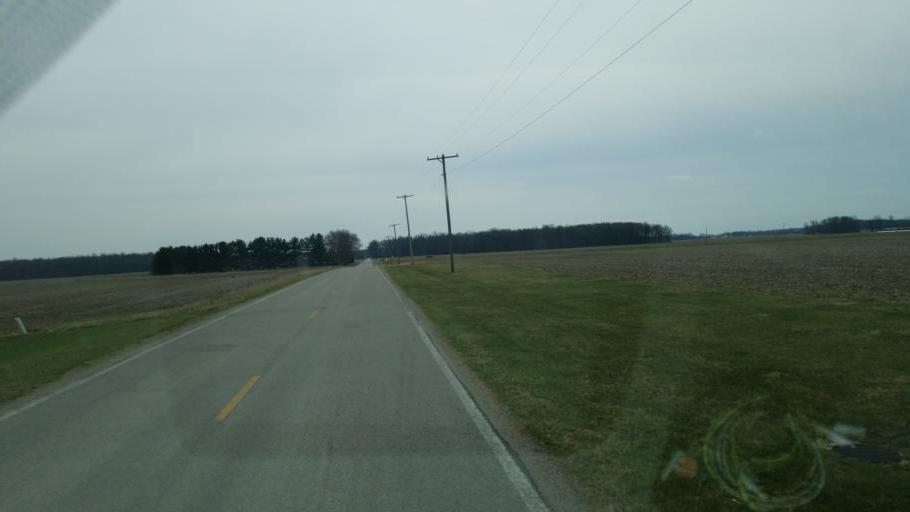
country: US
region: Ohio
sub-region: Huron County
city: New London
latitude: 41.1589
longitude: -82.4900
